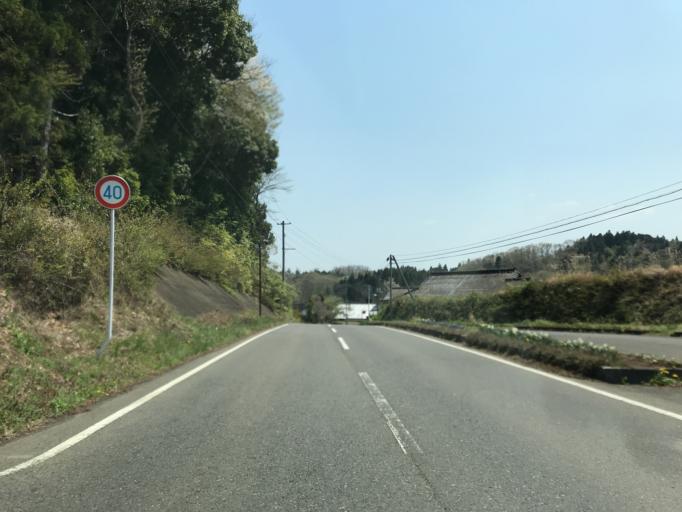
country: JP
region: Fukushima
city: Ishikawa
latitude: 37.1069
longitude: 140.3993
